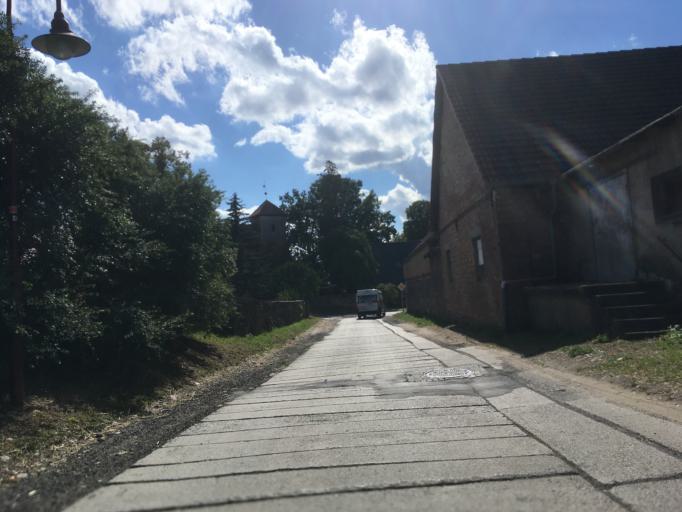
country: DE
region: Brandenburg
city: Angermunde
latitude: 52.9515
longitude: 14.0018
